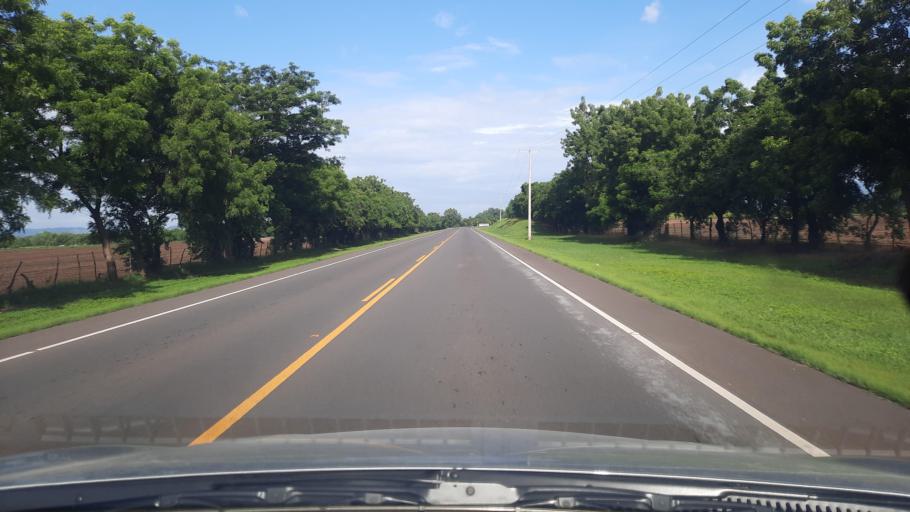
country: NI
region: Chinandega
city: Chichigalpa
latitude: 12.7644
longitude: -86.9029
